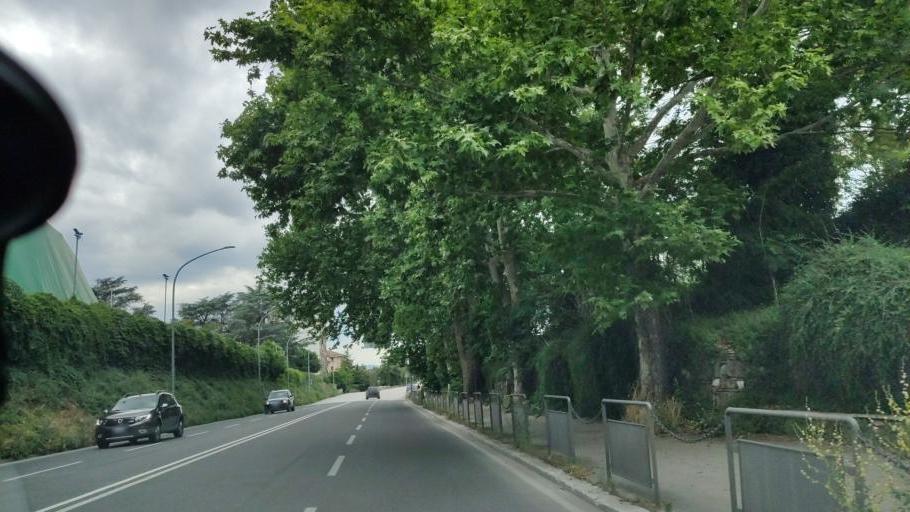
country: IT
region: Umbria
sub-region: Provincia di Terni
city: Terni
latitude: 42.5698
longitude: 12.6473
